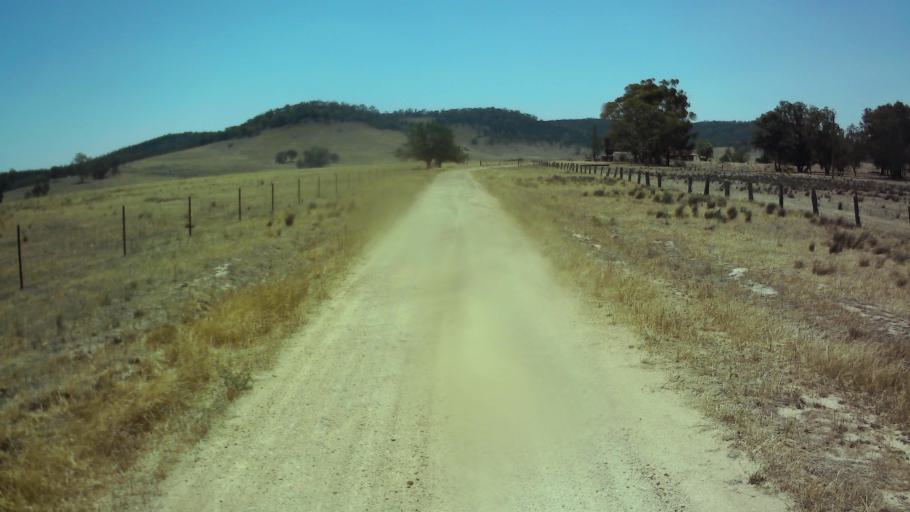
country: AU
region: New South Wales
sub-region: Weddin
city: Grenfell
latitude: -33.9133
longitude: 148.3217
